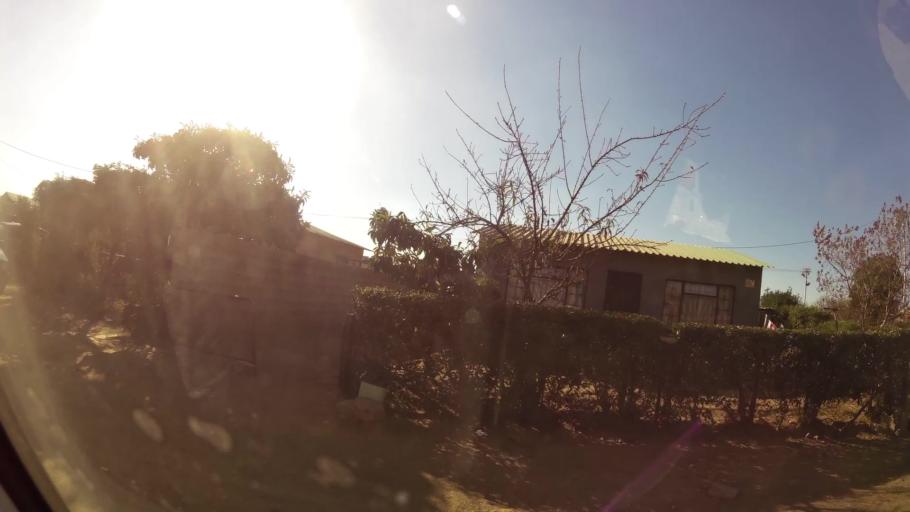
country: ZA
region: Gauteng
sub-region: City of Tshwane Metropolitan Municipality
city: Cullinan
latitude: -25.7163
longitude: 28.3852
